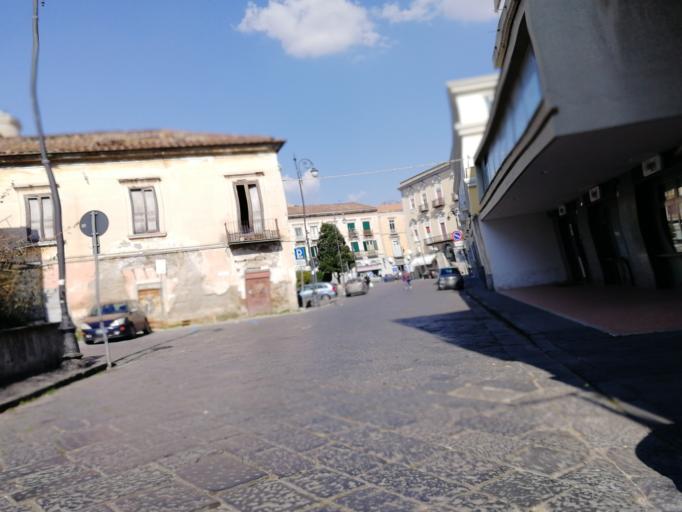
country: IT
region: Campania
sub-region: Provincia di Caserta
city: Santa Maria Capua Vetere
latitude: 41.0809
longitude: 14.2590
